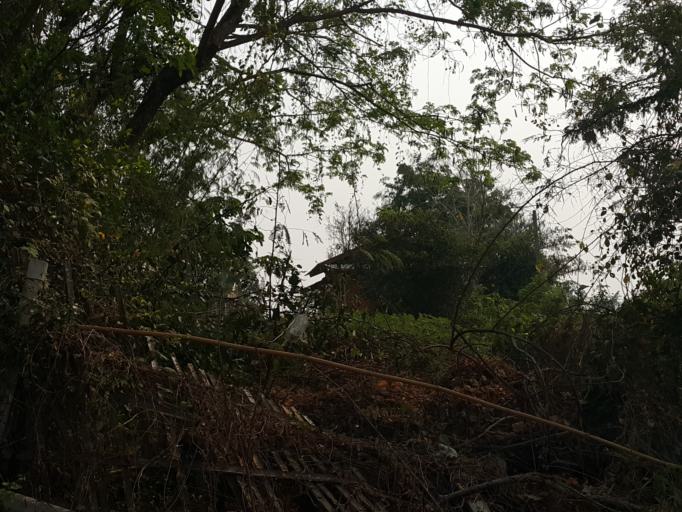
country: TH
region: Chiang Mai
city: San Kamphaeng
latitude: 18.7811
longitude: 99.1100
